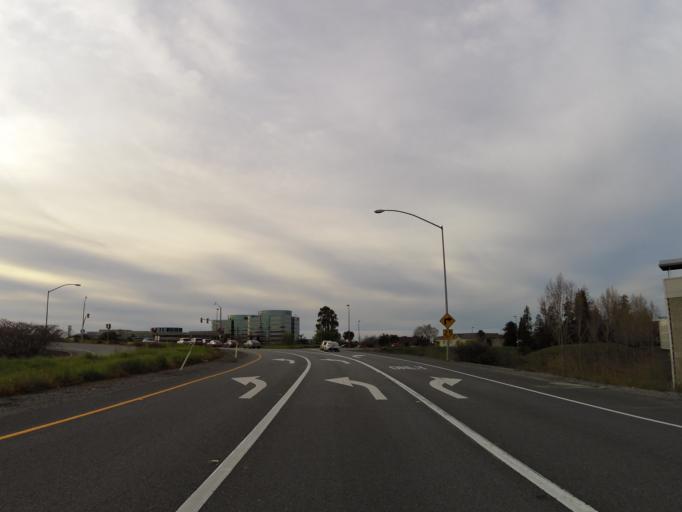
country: US
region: California
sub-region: Santa Clara County
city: Santa Clara
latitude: 37.3861
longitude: -121.9751
